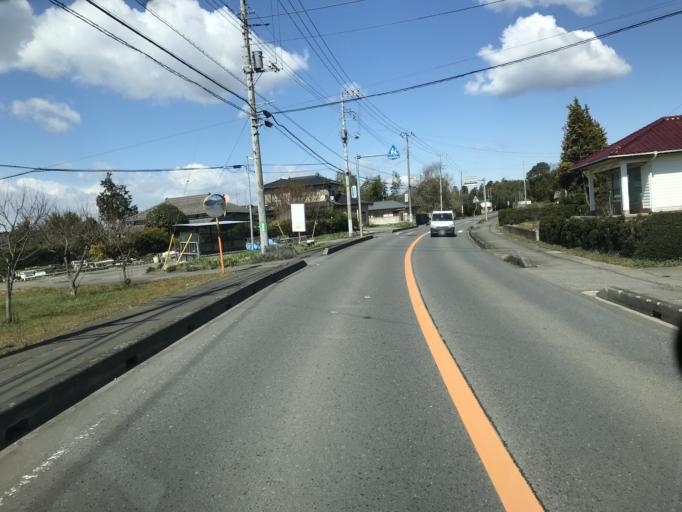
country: JP
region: Ibaraki
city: Ishioka
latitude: 36.0993
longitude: 140.2739
